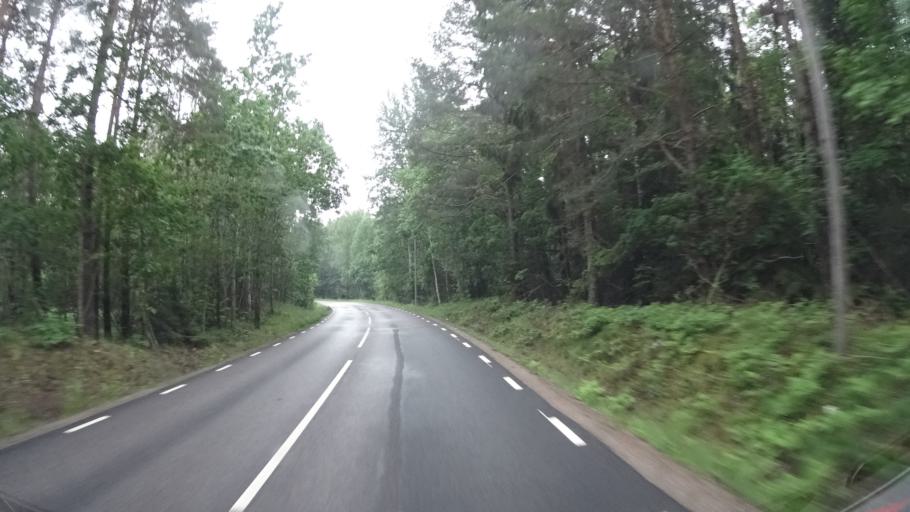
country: SE
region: Kalmar
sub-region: Oskarshamns Kommun
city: Oskarshamn
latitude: 57.3682
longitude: 16.2279
